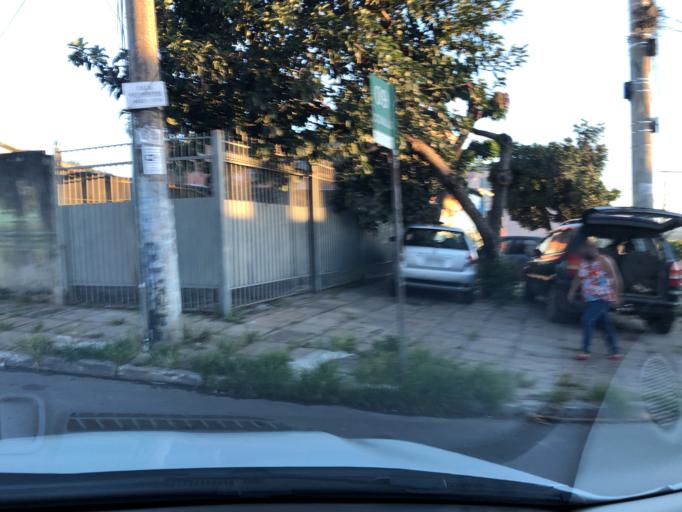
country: BR
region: Federal District
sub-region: Brasilia
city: Brasilia
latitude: -15.7753
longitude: -47.7826
